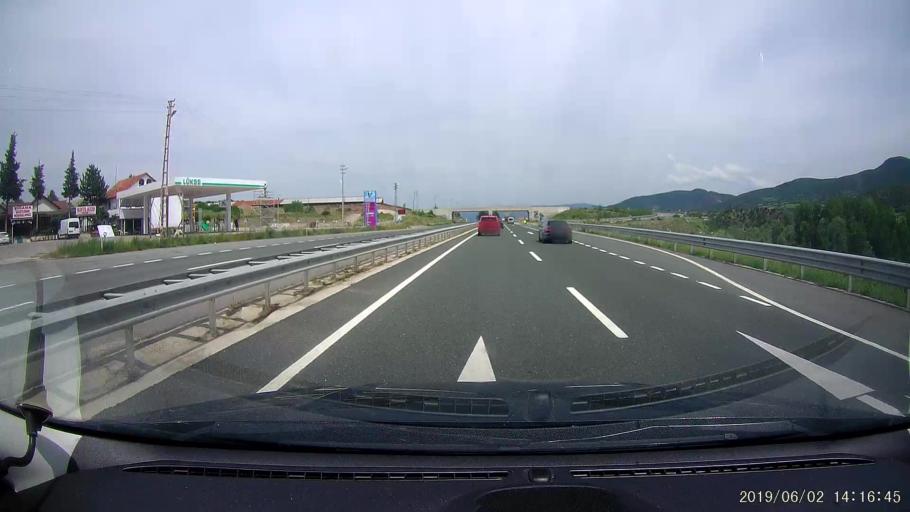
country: TR
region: Kastamonu
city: Tosya
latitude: 40.9507
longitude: 33.9166
